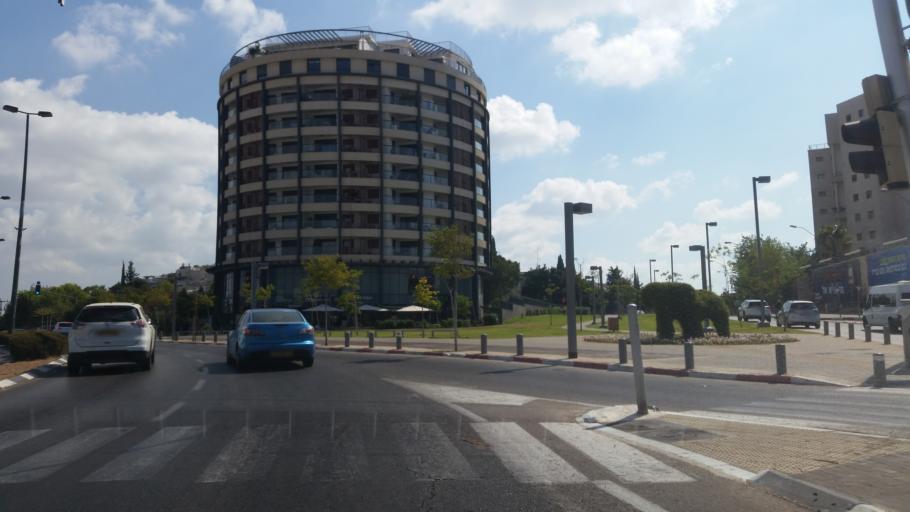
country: IL
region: Tel Aviv
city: Ramat HaSharon
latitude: 32.1239
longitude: 34.8241
